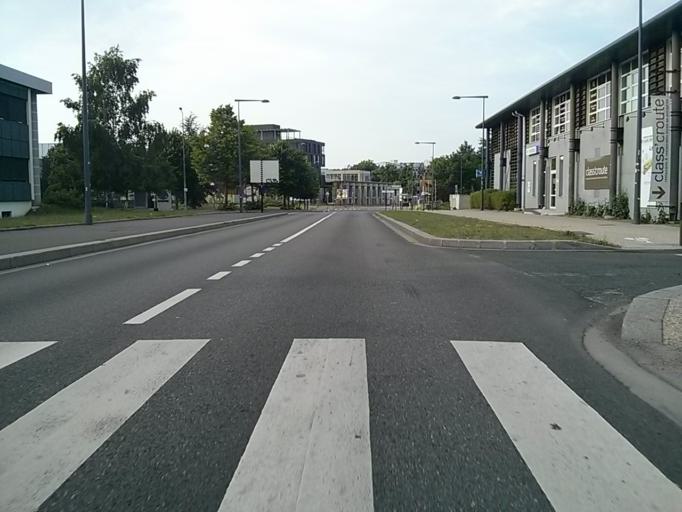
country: FR
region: Rhone-Alpes
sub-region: Departement de la Loire
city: Saint-Etienne
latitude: 45.4549
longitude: 4.3913
